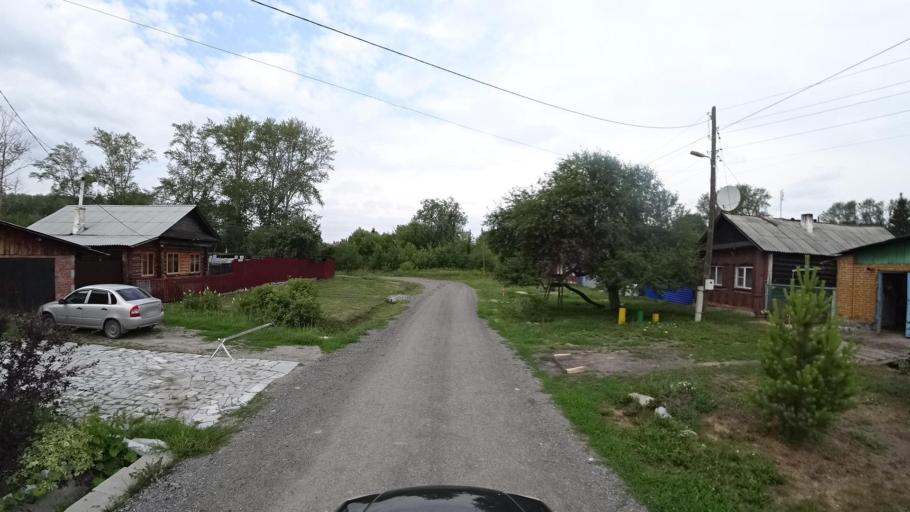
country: RU
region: Sverdlovsk
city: Kamyshlov
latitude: 56.8489
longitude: 62.6891
